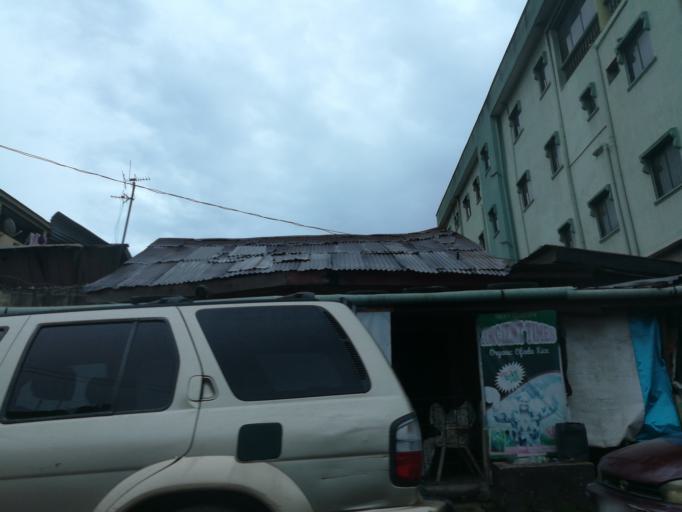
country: NG
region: Lagos
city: Makoko
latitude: 6.4928
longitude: 3.3794
